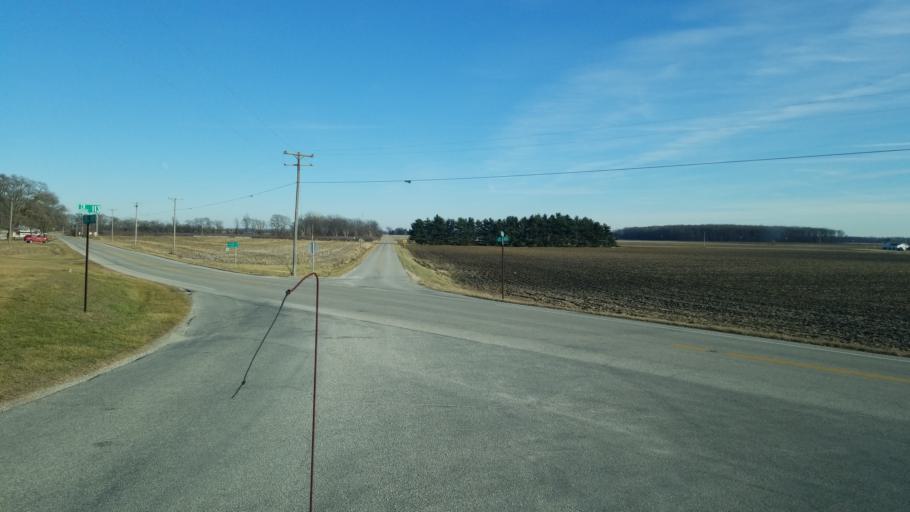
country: US
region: Ohio
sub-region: Sandusky County
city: Mount Carmel
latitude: 41.2561
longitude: -82.9798
